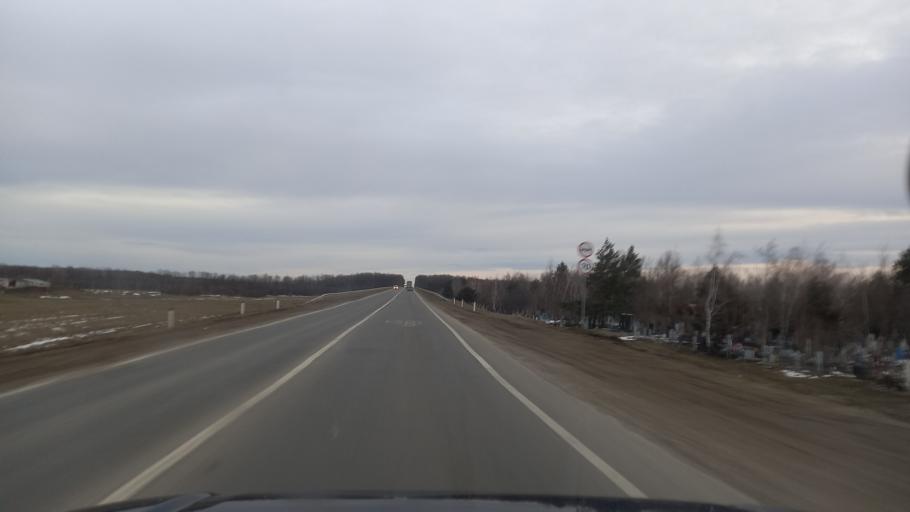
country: RU
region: Krasnodarskiy
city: Belorechensk
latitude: 44.7666
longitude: 39.9122
